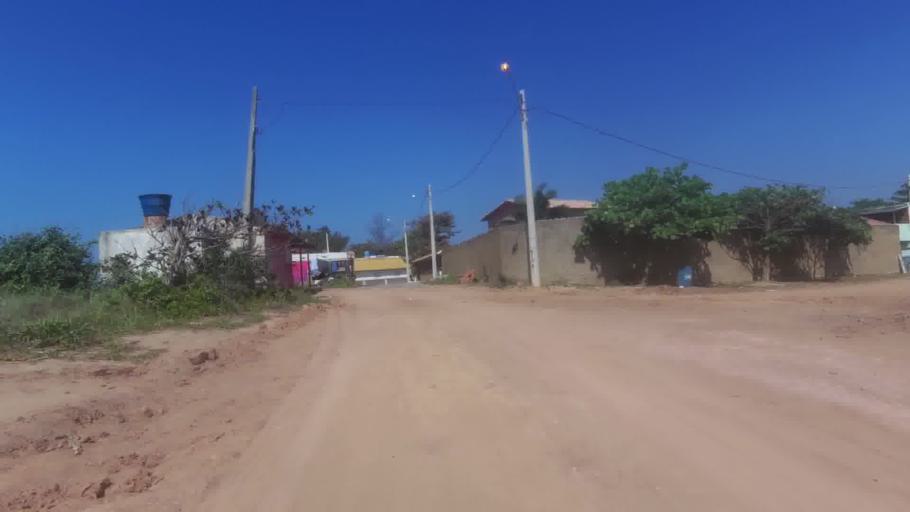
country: BR
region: Espirito Santo
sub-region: Marataizes
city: Marataizes
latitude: -21.0887
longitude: -40.8430
